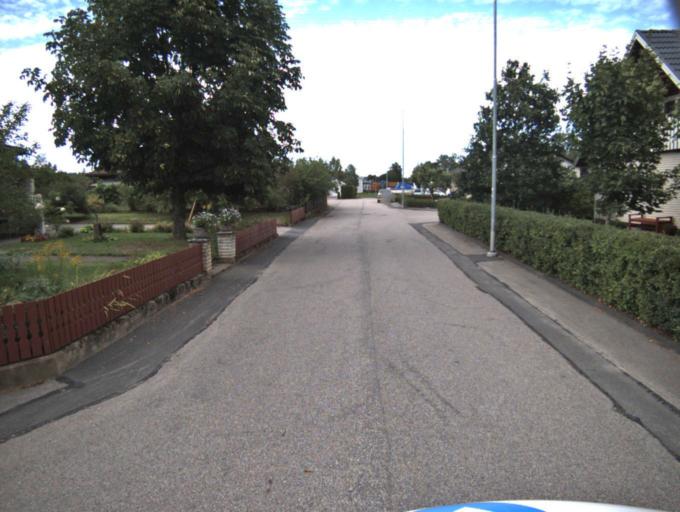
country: SE
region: Vaestra Goetaland
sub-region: Ulricehamns Kommun
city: Ulricehamn
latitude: 57.8617
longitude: 13.4262
